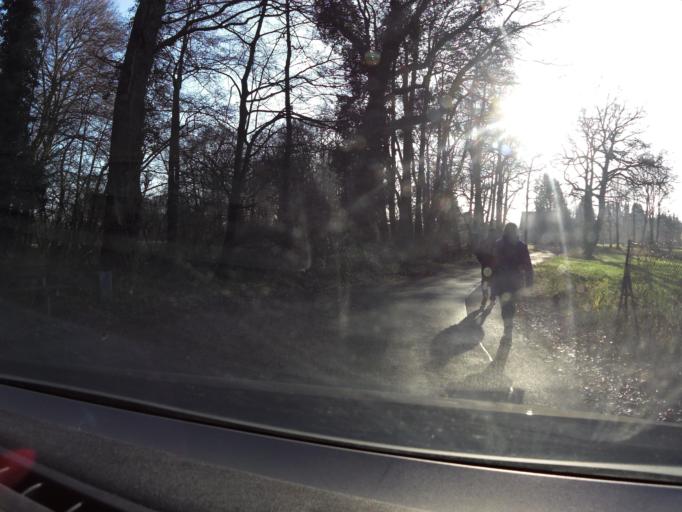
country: DE
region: North Rhine-Westphalia
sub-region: Regierungsbezirk Dusseldorf
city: Nettetal
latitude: 51.3398
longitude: 6.2600
